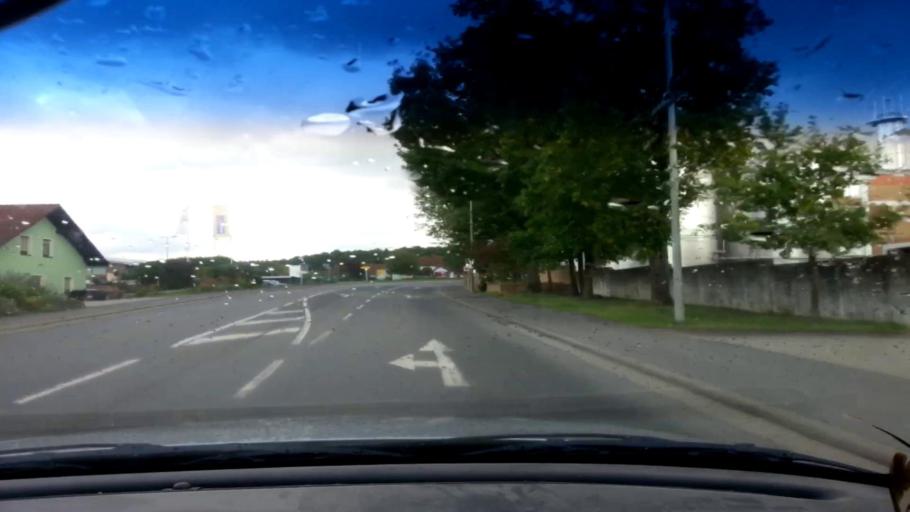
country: DE
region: Bavaria
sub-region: Upper Franconia
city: Zapfendorf
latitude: 50.0156
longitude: 10.9376
